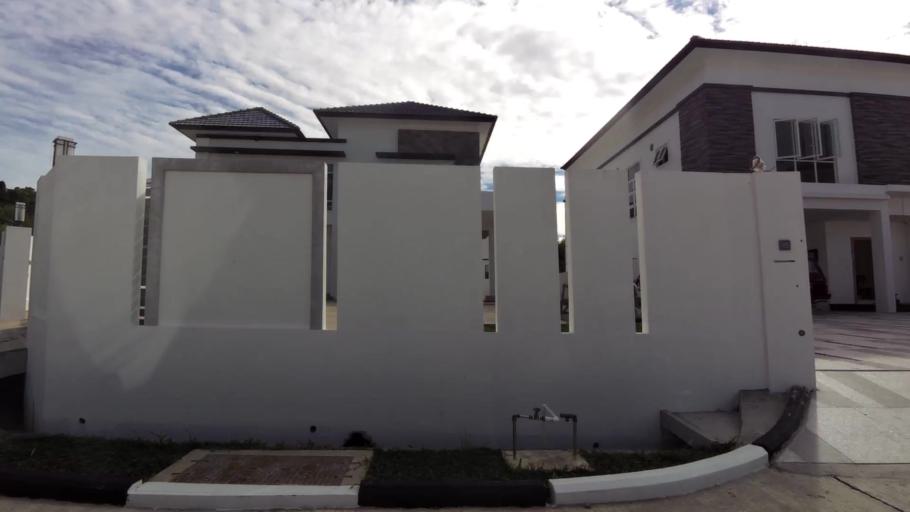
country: BN
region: Brunei and Muara
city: Bandar Seri Begawan
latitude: 4.9004
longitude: 114.9683
